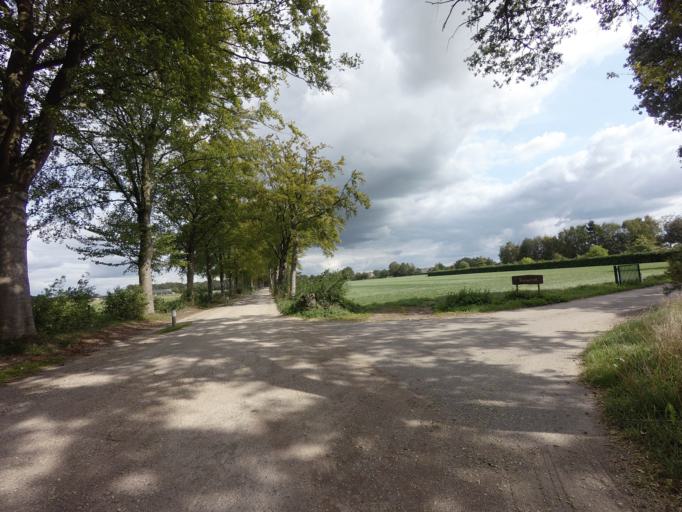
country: NL
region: Overijssel
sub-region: Gemeente Deventer
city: Schalkhaar
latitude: 52.2868
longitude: 6.2504
